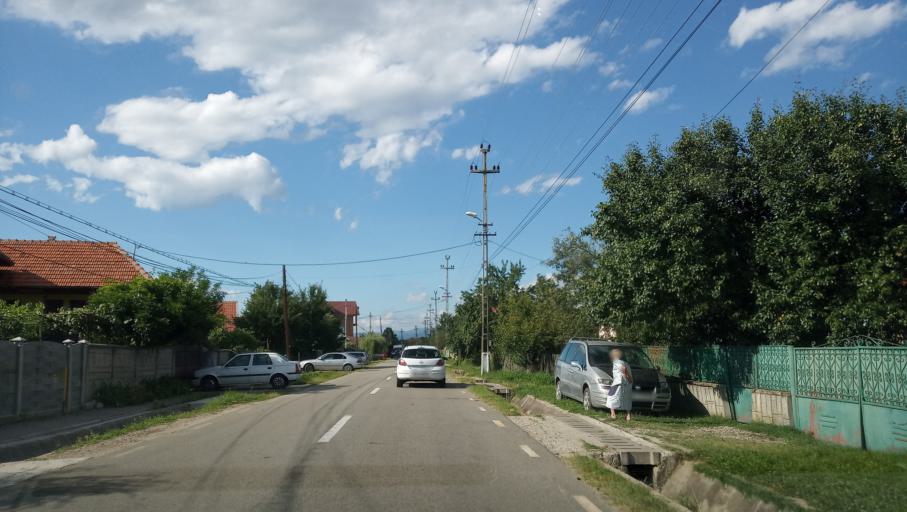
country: RO
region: Gorj
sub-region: Comuna Turcinesti
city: Turcinesti
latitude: 45.0560
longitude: 23.3475
